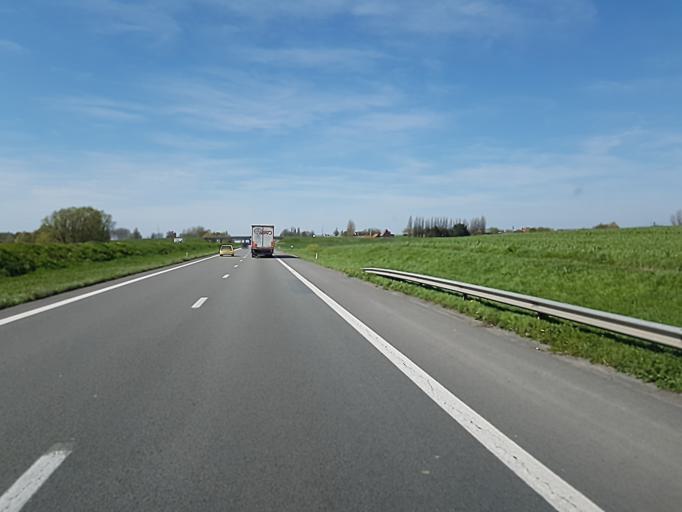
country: BE
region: Flanders
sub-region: Provincie West-Vlaanderen
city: Kortrijk
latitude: 50.7759
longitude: 3.2586
